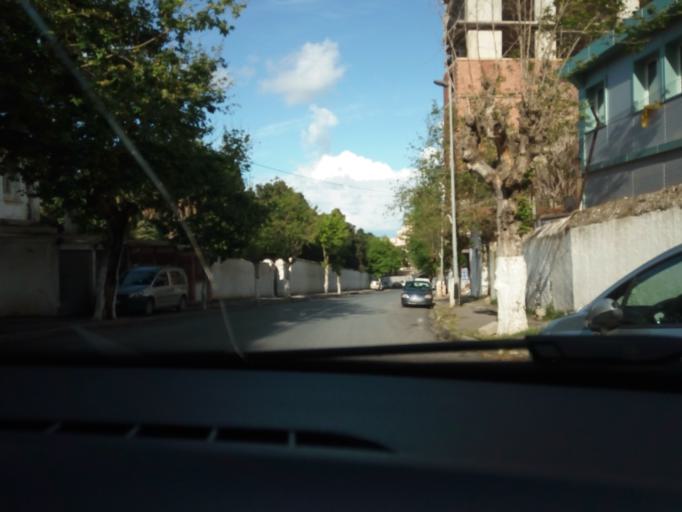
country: DZ
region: Alger
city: Algiers
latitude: 36.7967
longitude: 3.0472
